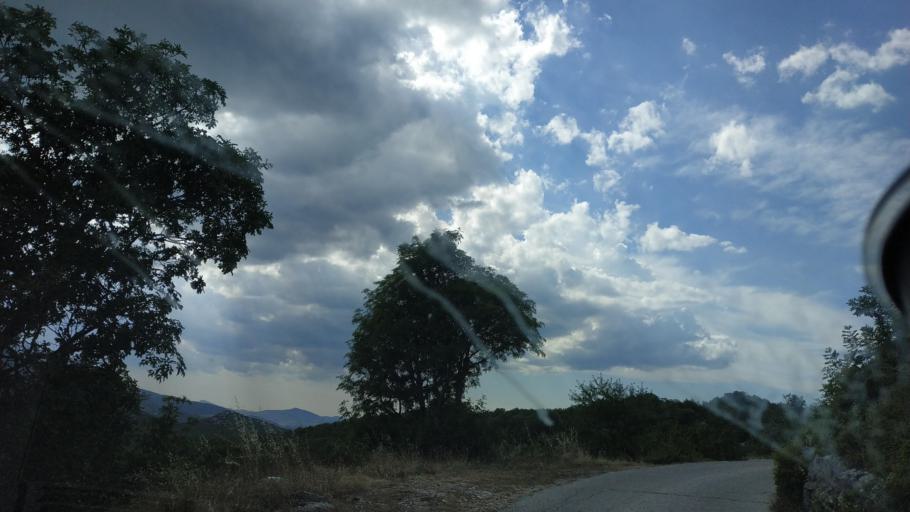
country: HR
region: Splitsko-Dalmatinska
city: Dugopolje
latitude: 43.5669
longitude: 16.6535
